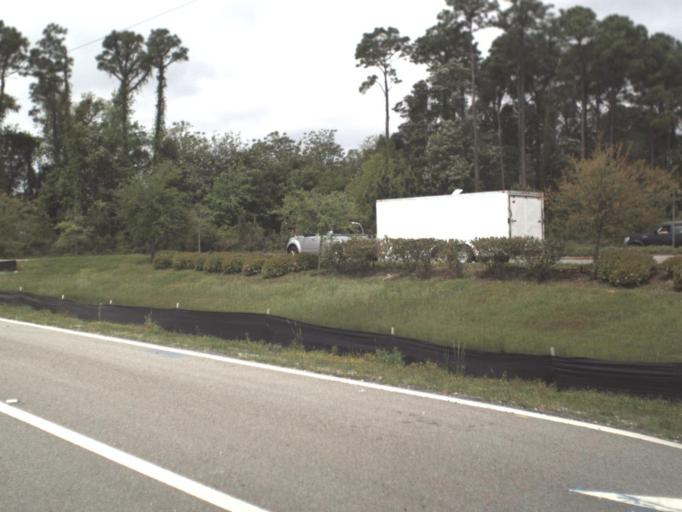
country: US
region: Florida
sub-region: Santa Rosa County
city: Tiger Point
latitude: 30.3905
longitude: -87.0629
